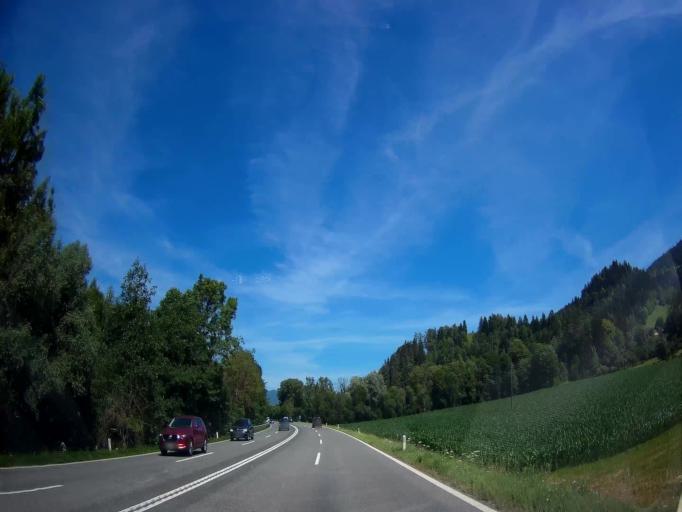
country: AT
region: Carinthia
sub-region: Politischer Bezirk Sankt Veit an der Glan
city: Micheldorf
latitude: 46.9133
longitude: 14.4374
